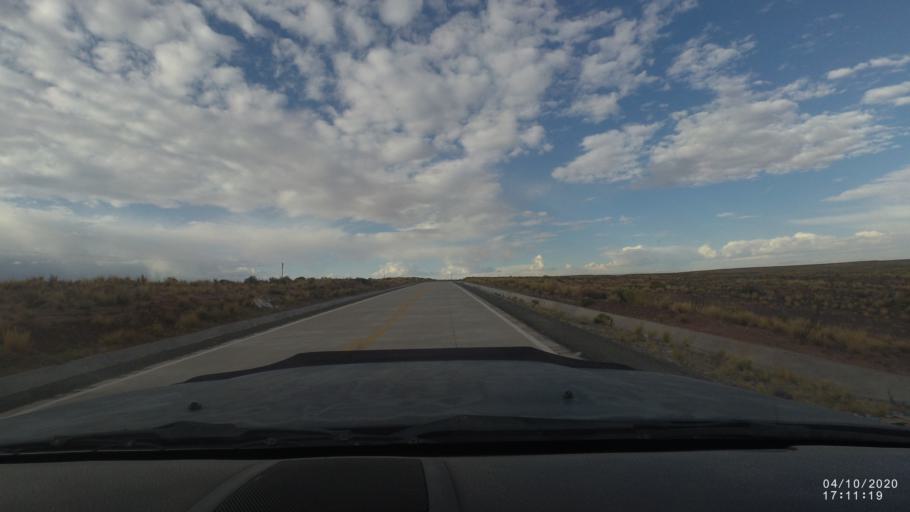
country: BO
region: Oruro
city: Oruro
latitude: -18.3211
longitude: -67.5773
